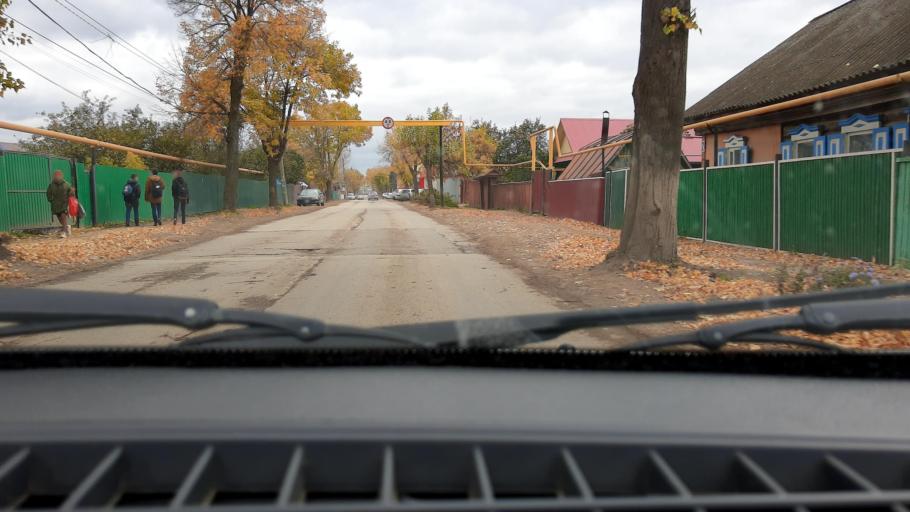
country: RU
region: Bashkortostan
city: Mikhaylovka
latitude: 54.7396
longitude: 55.8992
